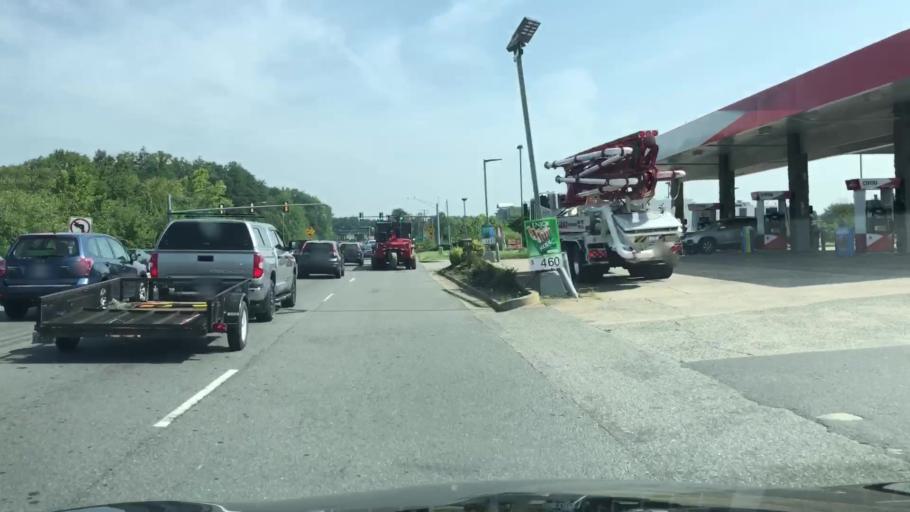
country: US
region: Virginia
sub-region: City of Fredericksburg
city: Fredericksburg
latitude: 38.2340
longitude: -77.5025
